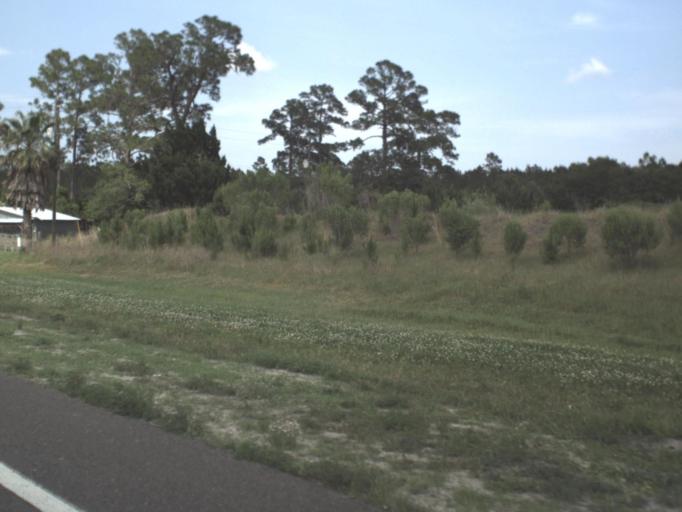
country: US
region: Florida
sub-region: Putnam County
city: East Palatka
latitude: 29.7516
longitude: -81.4681
